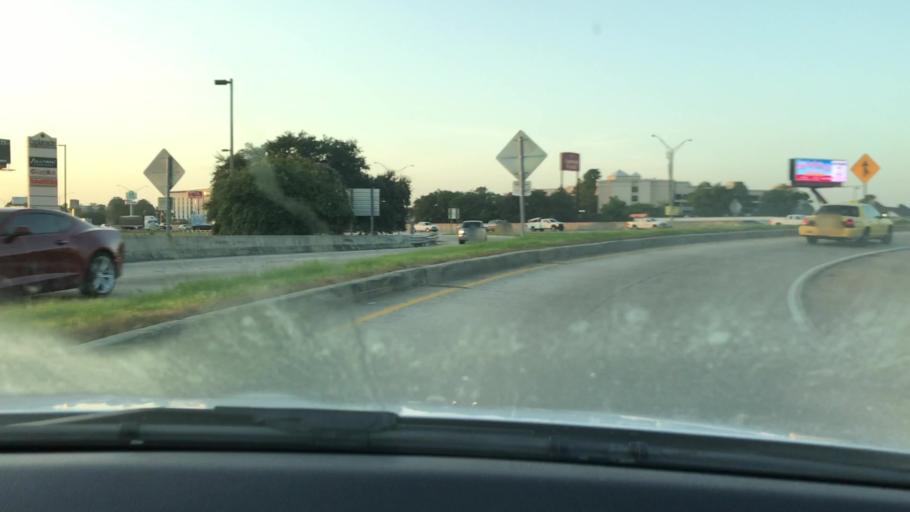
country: US
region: Louisiana
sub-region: East Baton Rouge Parish
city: Baton Rouge
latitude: 30.4238
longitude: -91.1378
